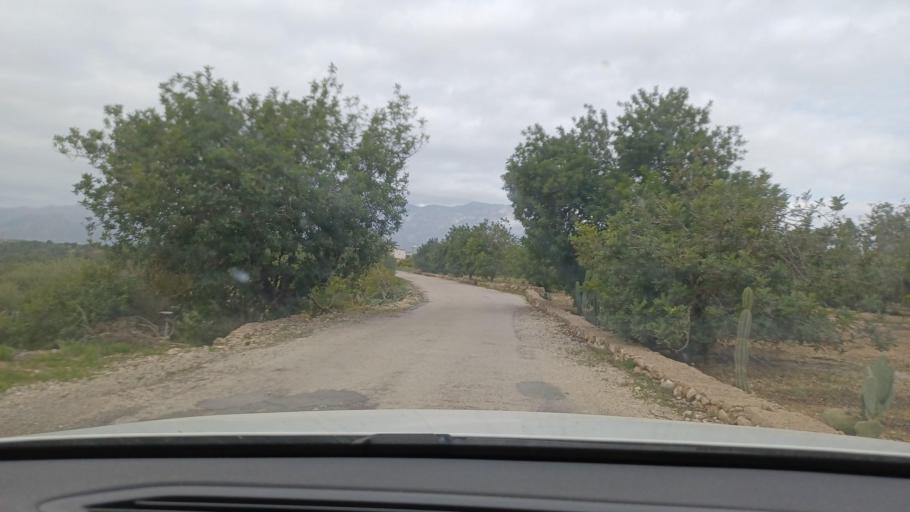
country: ES
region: Catalonia
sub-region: Provincia de Tarragona
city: Tortosa
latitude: 40.7908
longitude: 0.4855
